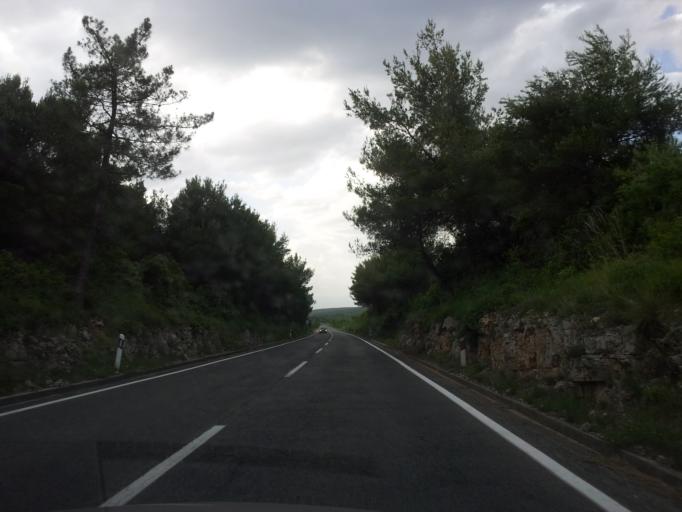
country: HR
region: Zadarska
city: Sukosan
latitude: 44.0118
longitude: 15.3632
